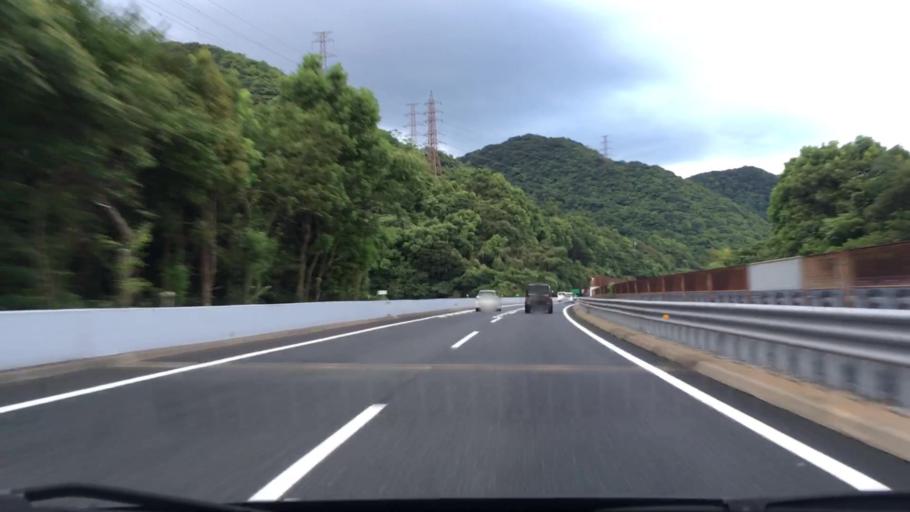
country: JP
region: Fukuoka
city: Kanda
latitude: 33.8590
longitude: 130.9396
